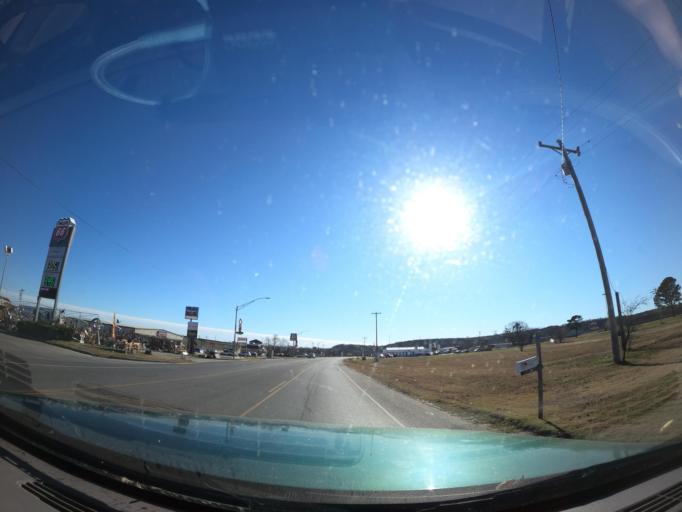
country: US
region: Oklahoma
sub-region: McIntosh County
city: Eufaula
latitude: 35.2802
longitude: -95.5829
